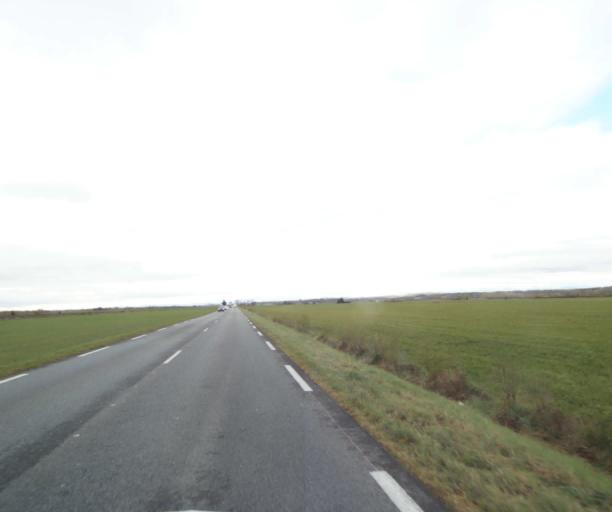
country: FR
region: Midi-Pyrenees
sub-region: Departement de l'Ariege
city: Saverdun
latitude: 43.2694
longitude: 1.5524
